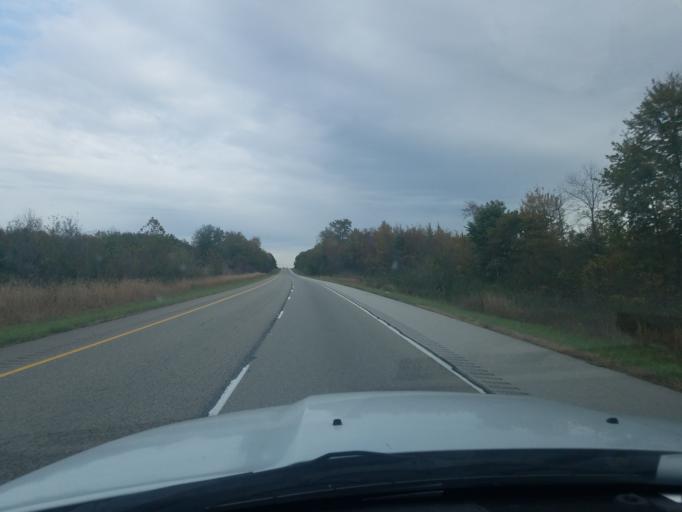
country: US
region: Indiana
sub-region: Spencer County
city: Dale
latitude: 38.1964
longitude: -87.1361
